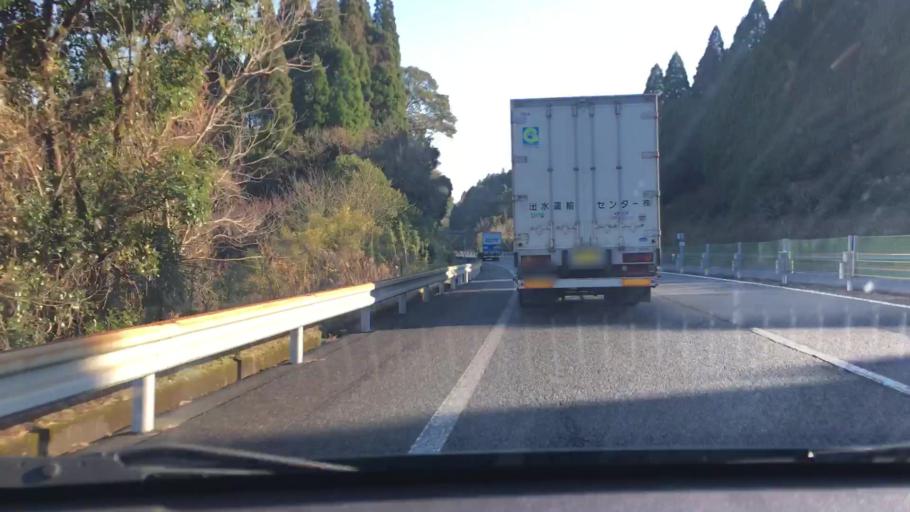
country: JP
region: Kagoshima
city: Kajiki
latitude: 31.8353
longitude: 130.6903
